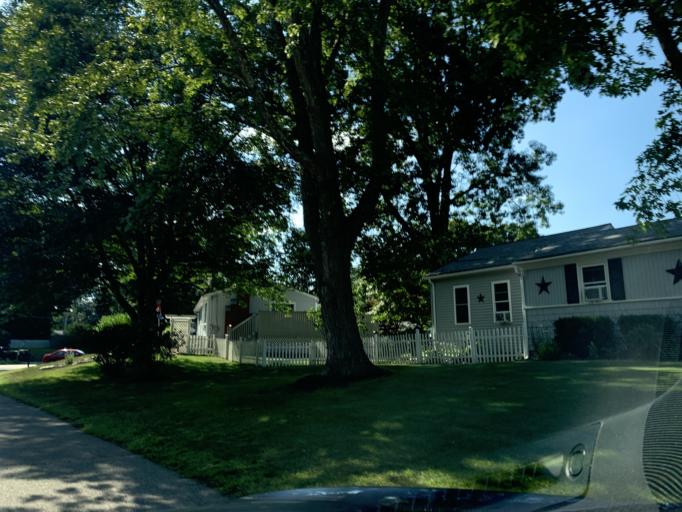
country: US
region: Rhode Island
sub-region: Kent County
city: East Greenwich
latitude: 41.6182
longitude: -71.4519
